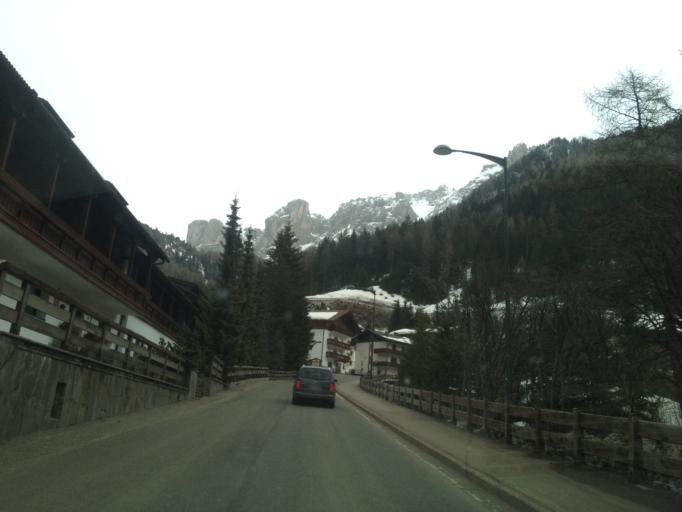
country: IT
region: Trentino-Alto Adige
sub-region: Bolzano
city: Selva
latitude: 46.5460
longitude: 11.7697
